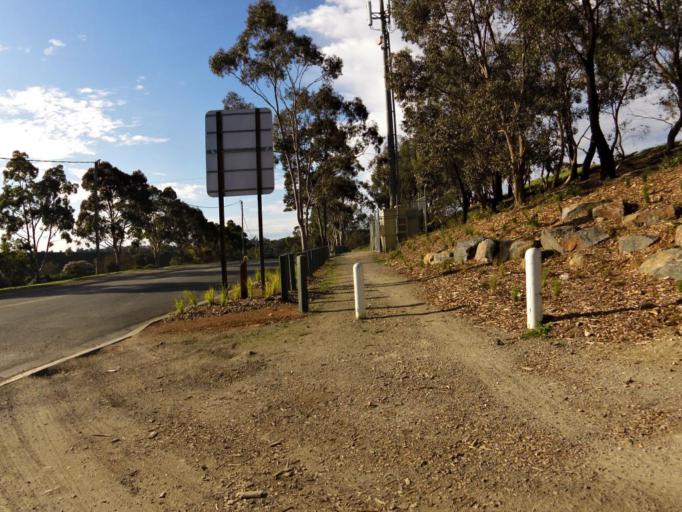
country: AU
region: Victoria
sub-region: Whitehorse
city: Vermont South
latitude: -37.8610
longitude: 145.1978
